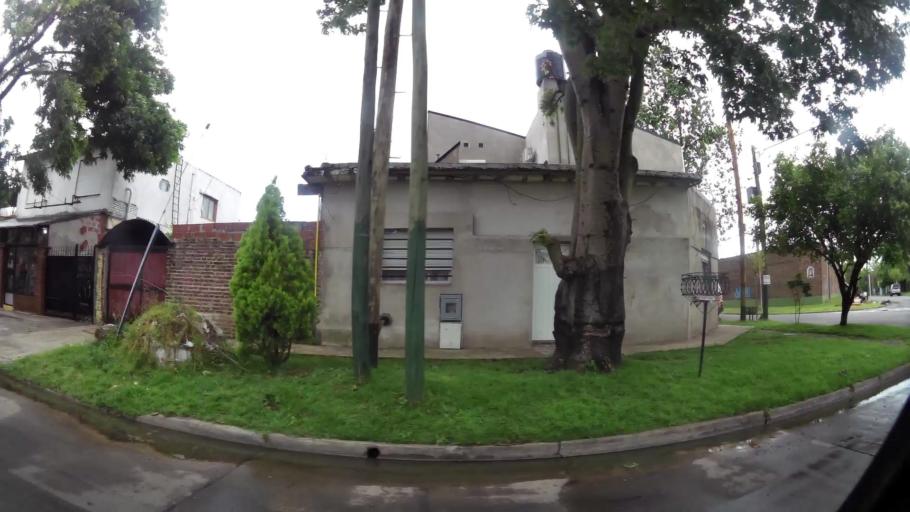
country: AR
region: Buenos Aires
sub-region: Partido de Lomas de Zamora
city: Lomas de Zamora
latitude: -34.7455
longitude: -58.3750
